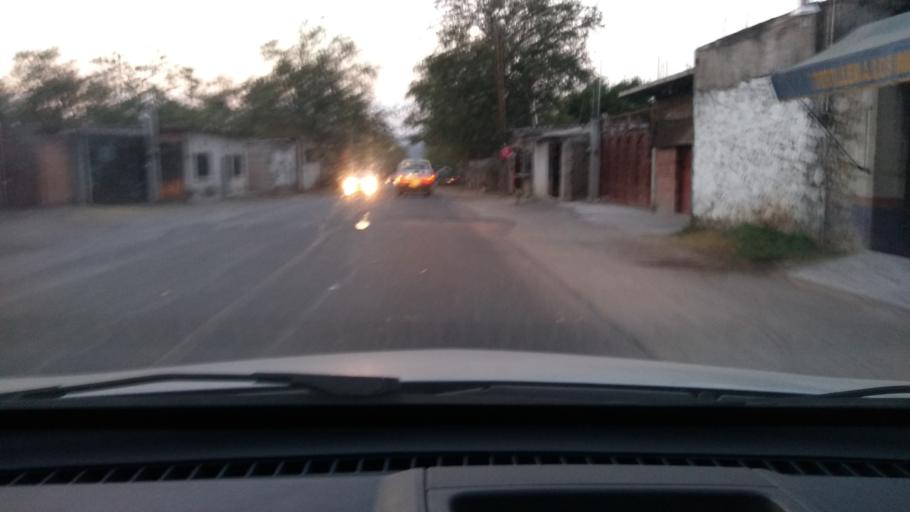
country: MX
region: Morelos
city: Coatetelco
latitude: 18.7270
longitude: -99.3180
